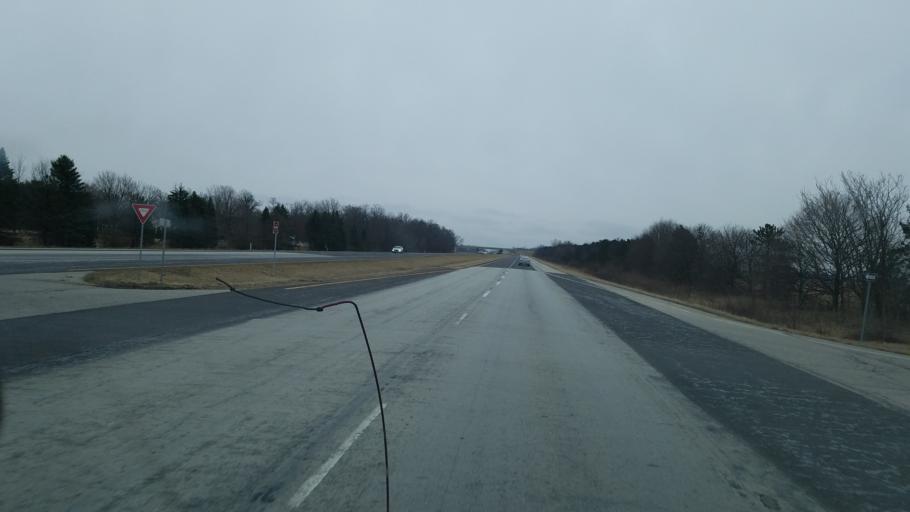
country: US
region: Indiana
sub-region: Fulton County
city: Rochester
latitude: 41.0599
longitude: -86.2401
